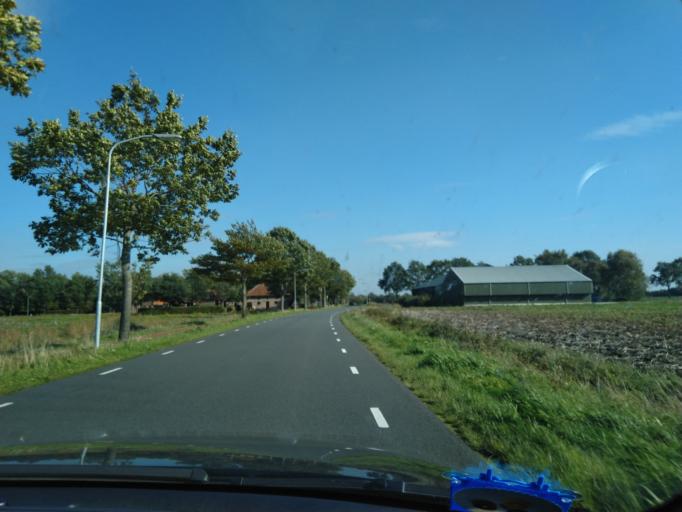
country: NL
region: Groningen
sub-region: Gemeente Veendam
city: Veendam
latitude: 53.0913
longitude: 6.8315
